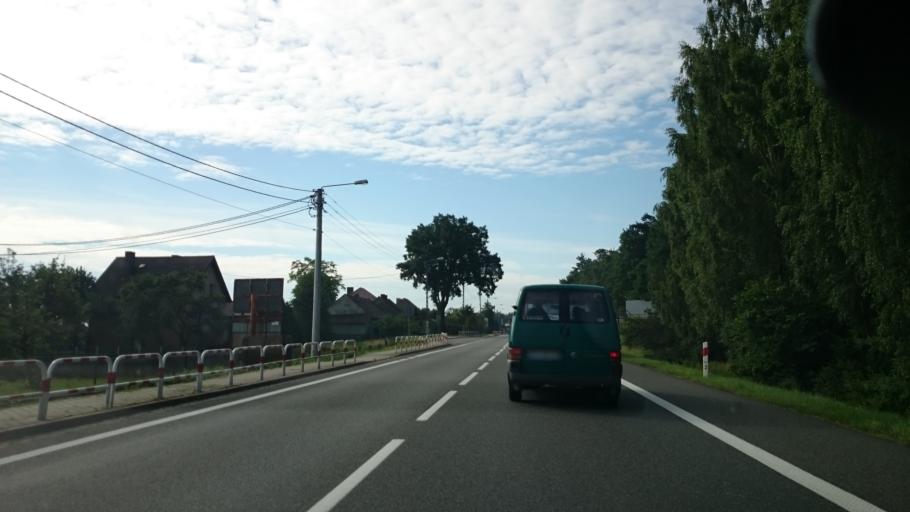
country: PL
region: Opole Voivodeship
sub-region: Powiat opolski
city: Tarnow Opolski
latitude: 50.6088
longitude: 18.0713
